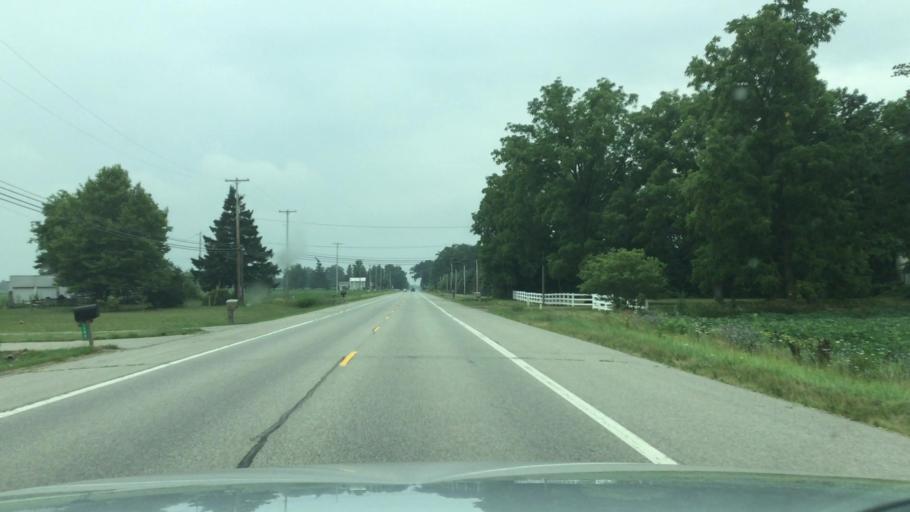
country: US
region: Michigan
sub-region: Shiawassee County
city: Owosso
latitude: 43.0472
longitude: -84.1771
